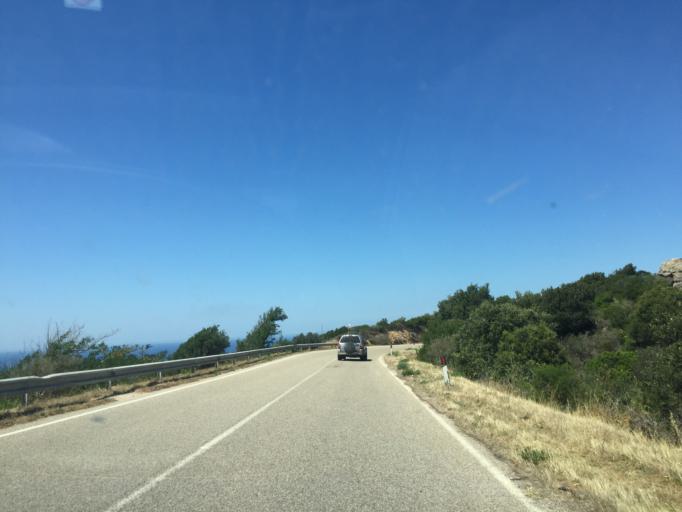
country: IT
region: Sardinia
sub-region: Provincia di Olbia-Tempio
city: Aglientu
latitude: 41.0927
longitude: 9.0968
